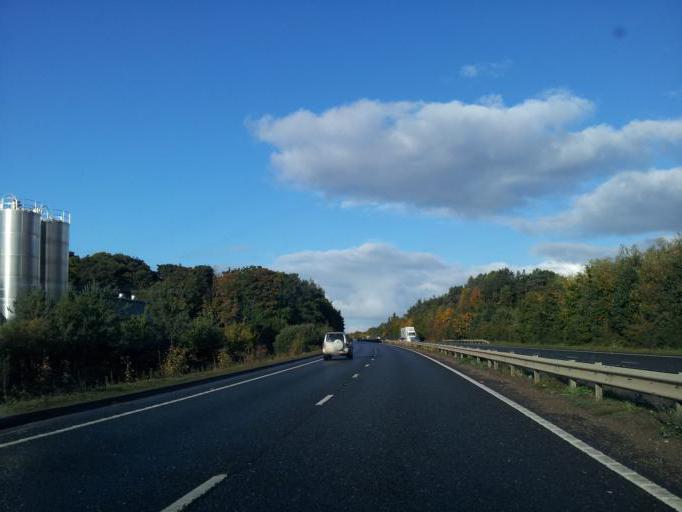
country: GB
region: England
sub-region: Norfolk
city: Costessey
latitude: 52.6535
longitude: 1.1759
